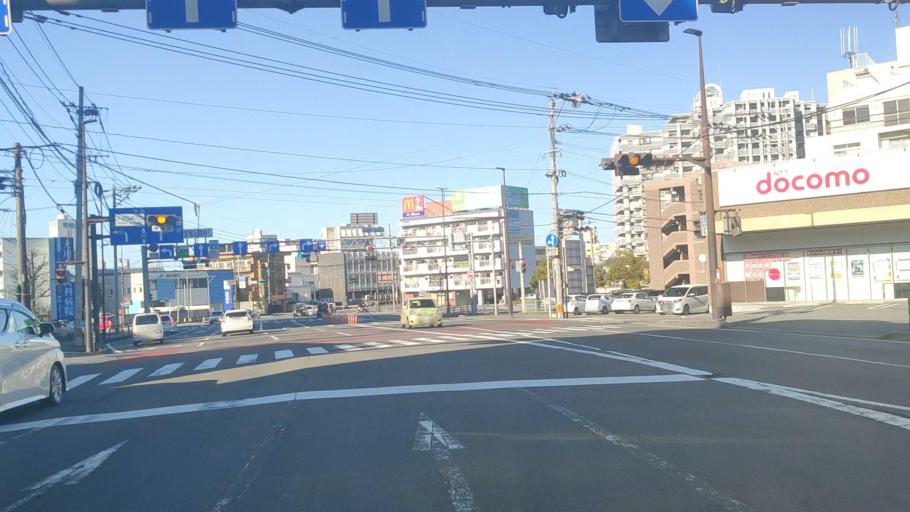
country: JP
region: Oita
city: Oita
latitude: 33.2250
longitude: 131.5956
